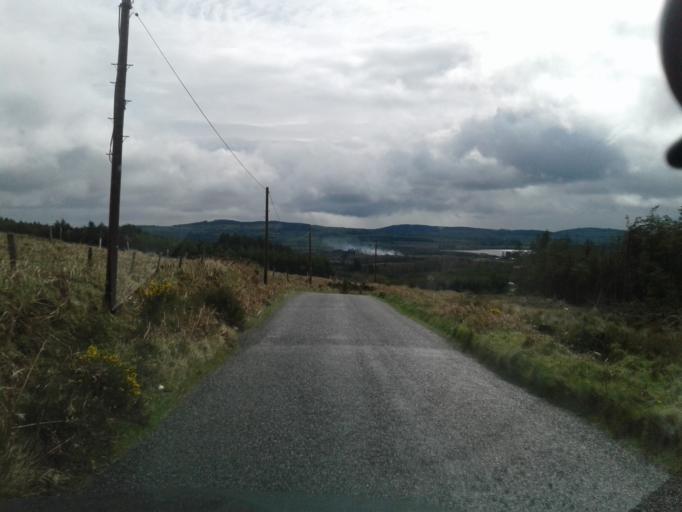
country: IE
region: Leinster
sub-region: Wicklow
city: Enniskerry
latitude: 53.0929
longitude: -6.2424
